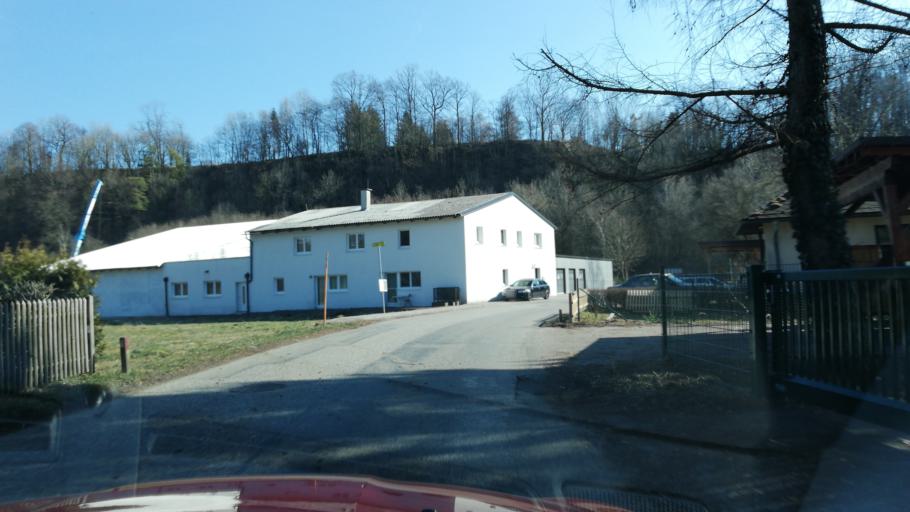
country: AT
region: Upper Austria
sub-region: Politischer Bezirk Vocklabruck
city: Redlham
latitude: 48.0139
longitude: 13.7498
